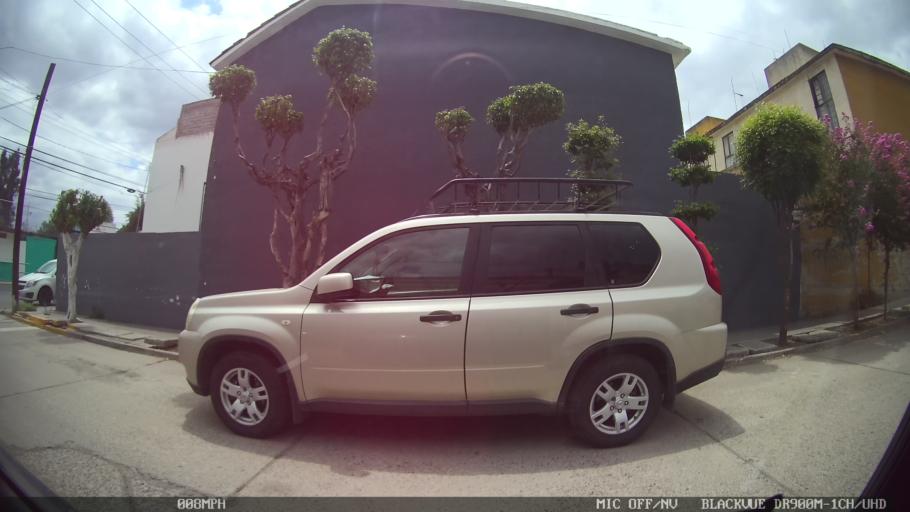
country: MX
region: Jalisco
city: Tonala
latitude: 20.6366
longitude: -103.2615
